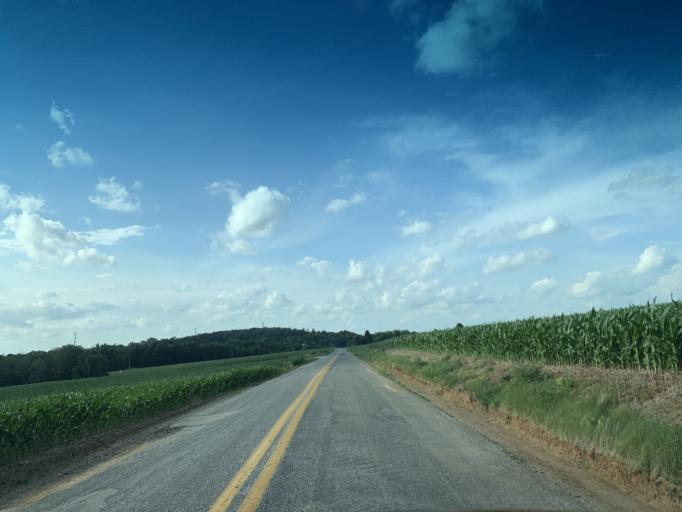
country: US
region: Pennsylvania
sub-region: York County
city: Stewartstown
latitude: 39.7427
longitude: -76.5429
